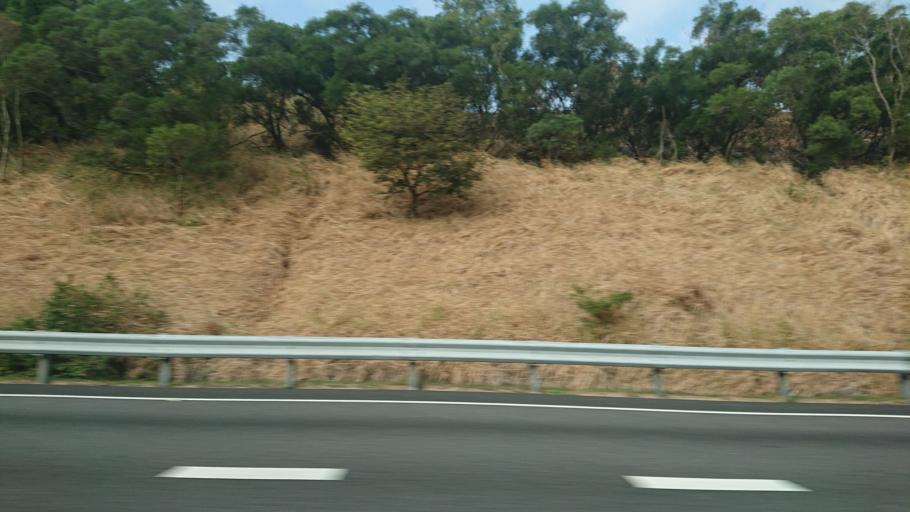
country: TW
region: Taiwan
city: Fengyuan
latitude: 24.2945
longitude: 120.6021
